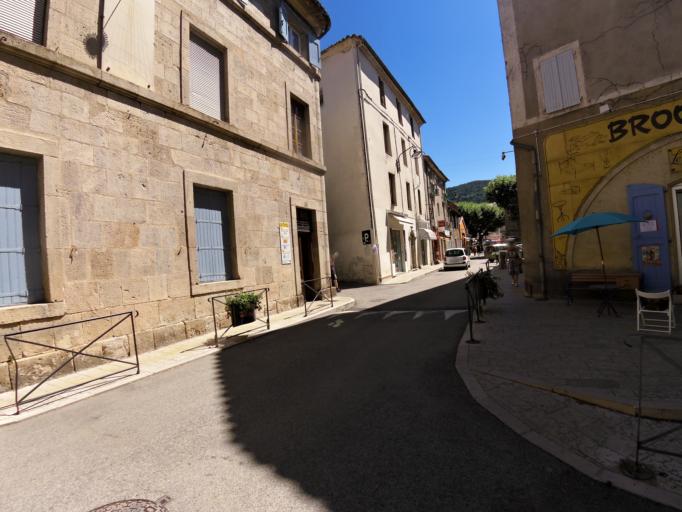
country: FR
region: Languedoc-Roussillon
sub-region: Departement du Gard
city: Saint-Jean-du-Gard
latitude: 44.1053
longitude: 3.8835
